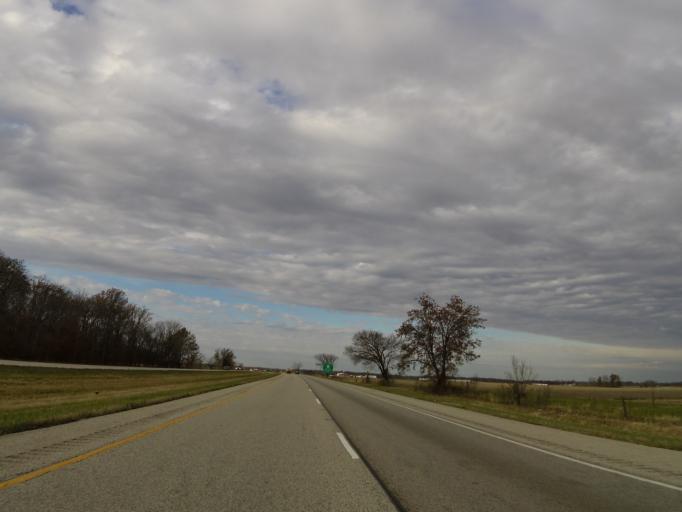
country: US
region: Illinois
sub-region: Washington County
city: Nashville
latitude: 38.3913
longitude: -89.3444
